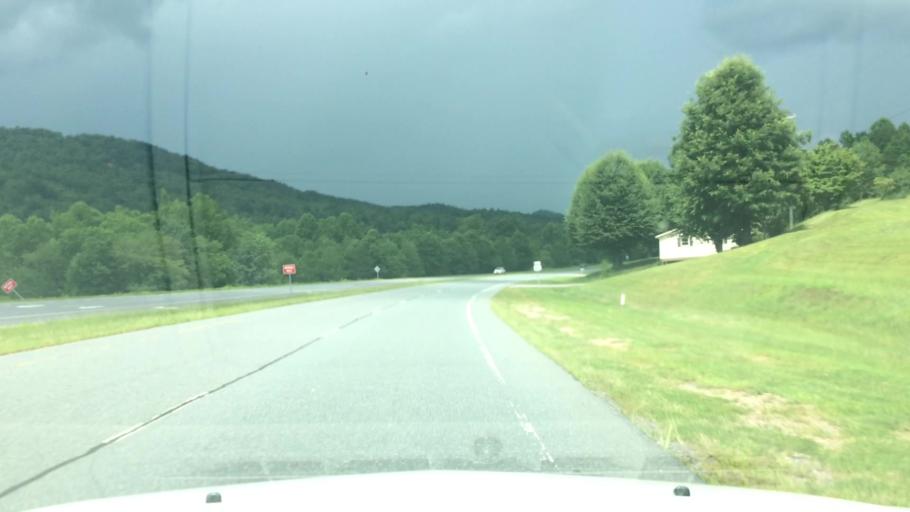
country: US
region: North Carolina
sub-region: Wilkes County
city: Millers Creek
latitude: 36.1593
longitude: -81.3645
